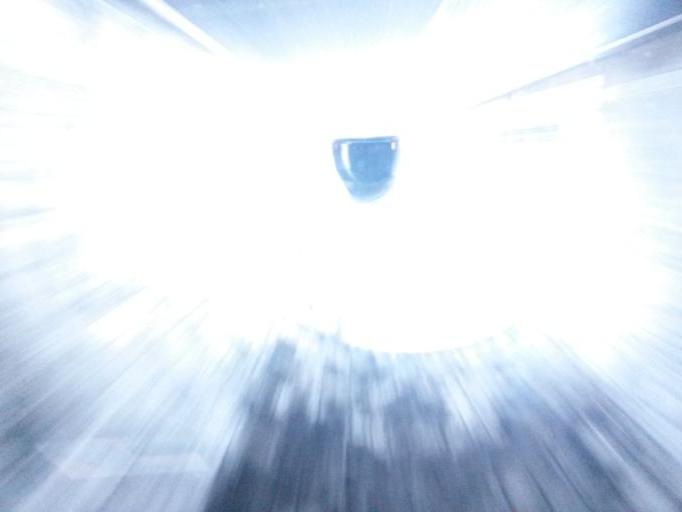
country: IT
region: Trentino-Alto Adige
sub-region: Provincia di Trento
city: Riva del Garda
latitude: 45.8578
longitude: 10.8326
